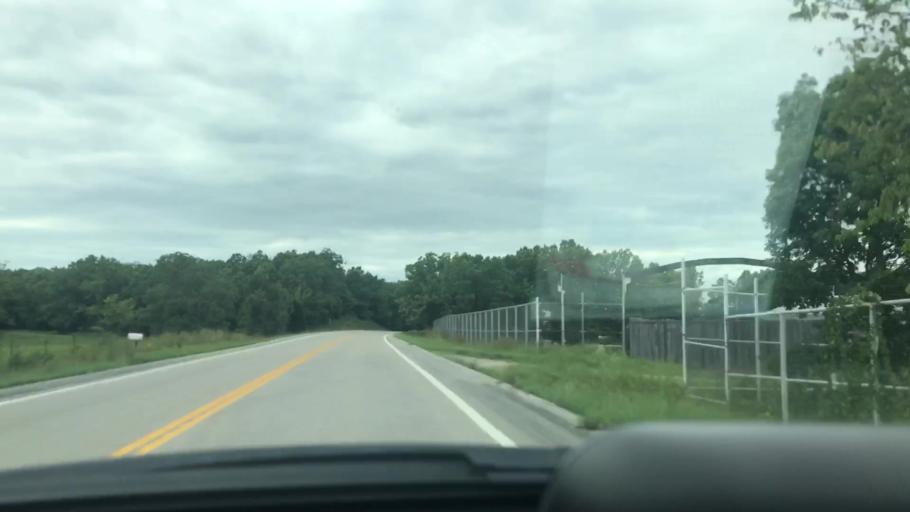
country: US
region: Missouri
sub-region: Benton County
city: Warsaw
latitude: 38.1644
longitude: -93.3063
